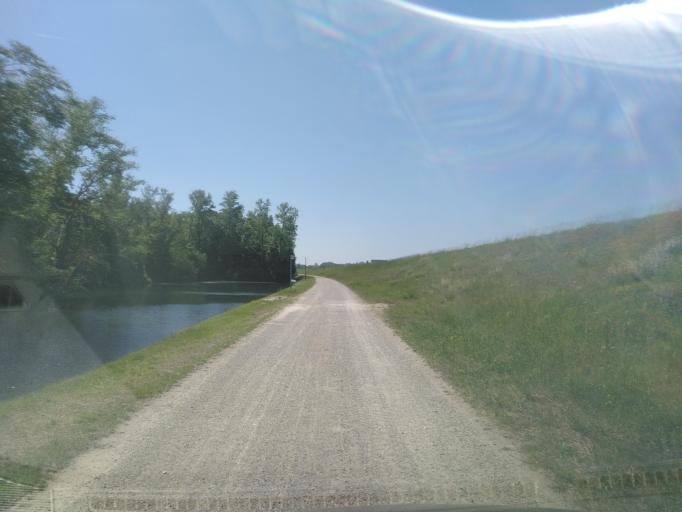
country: FR
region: Alsace
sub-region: Departement du Haut-Rhin
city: Kunheim
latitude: 48.0908
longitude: 7.5755
